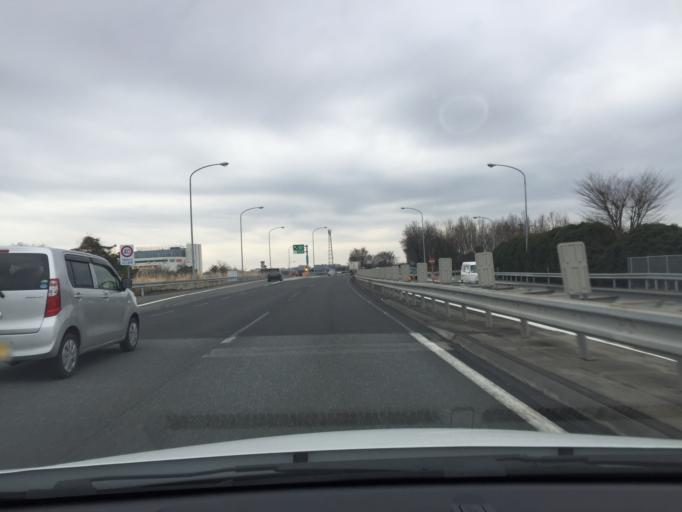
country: JP
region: Saitama
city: Sayama
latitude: 35.8679
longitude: 139.3776
